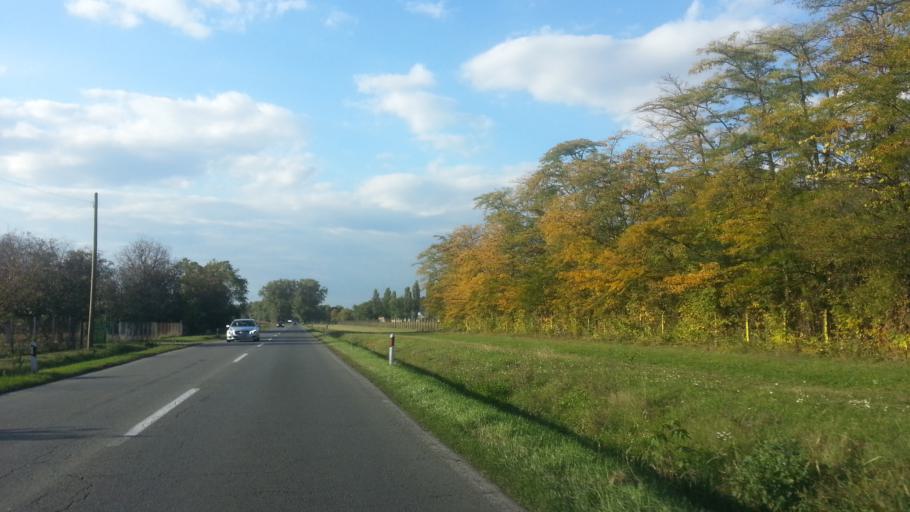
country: RS
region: Autonomna Pokrajina Vojvodina
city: Nova Pazova
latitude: 44.9201
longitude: 20.2515
